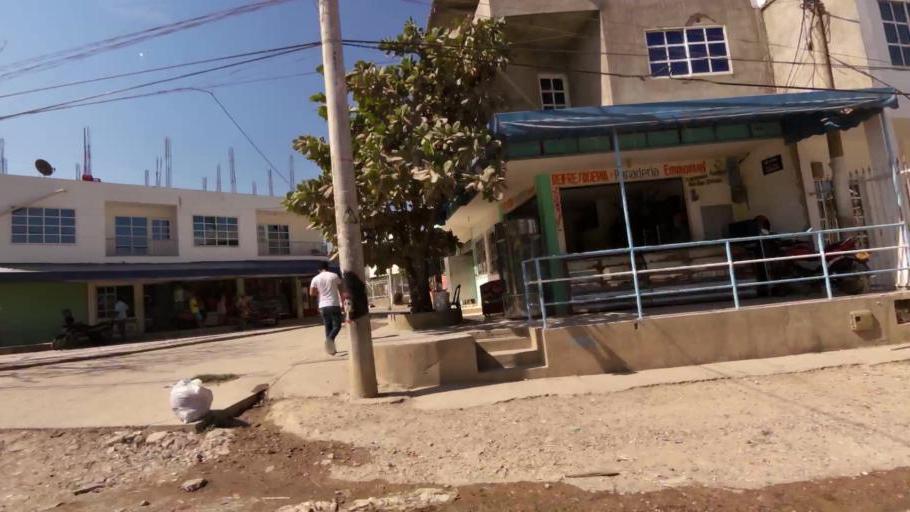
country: CO
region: Bolivar
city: Cartagena
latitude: 10.3745
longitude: -75.4967
